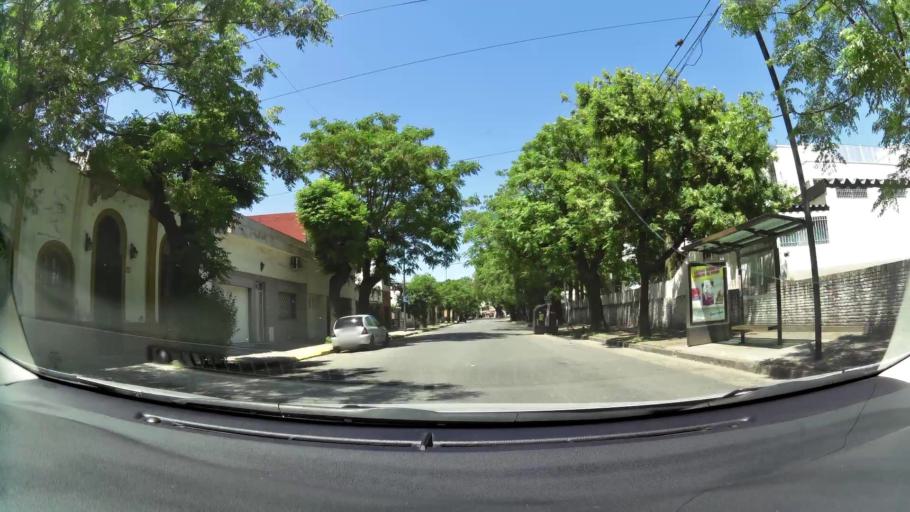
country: AR
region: Buenos Aires F.D.
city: Buenos Aires
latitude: -34.6430
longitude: -58.4094
